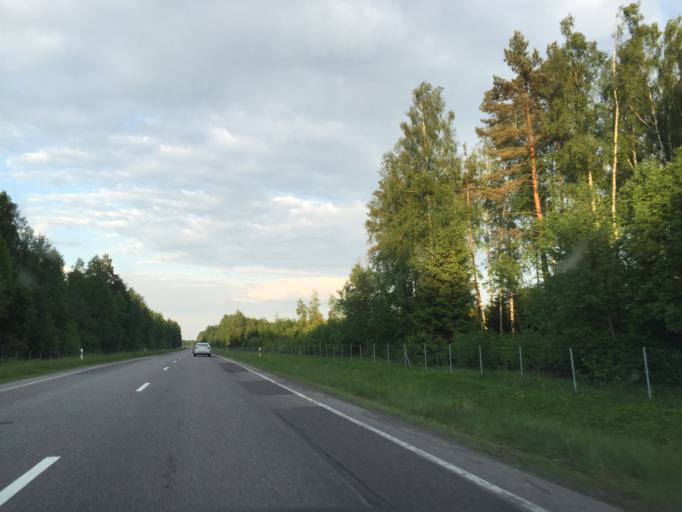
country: LT
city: Venta
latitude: 56.0003
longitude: 22.6258
